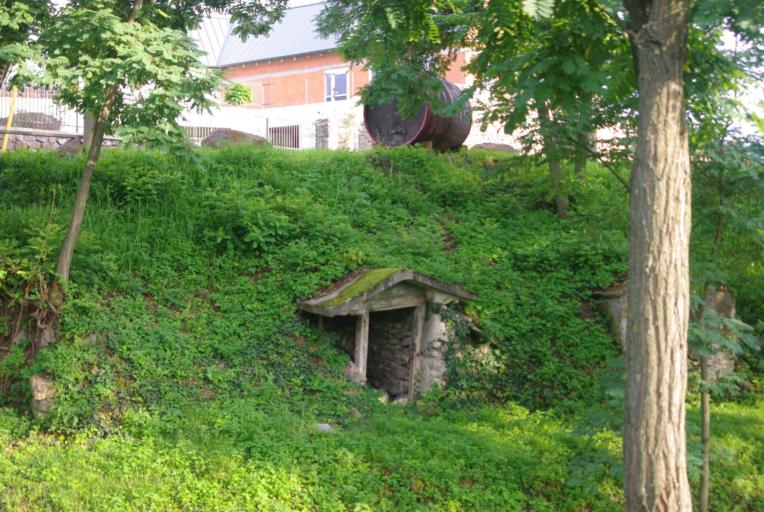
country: HU
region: Borsod-Abauj-Zemplen
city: Gonc
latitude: 48.3940
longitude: 21.2870
